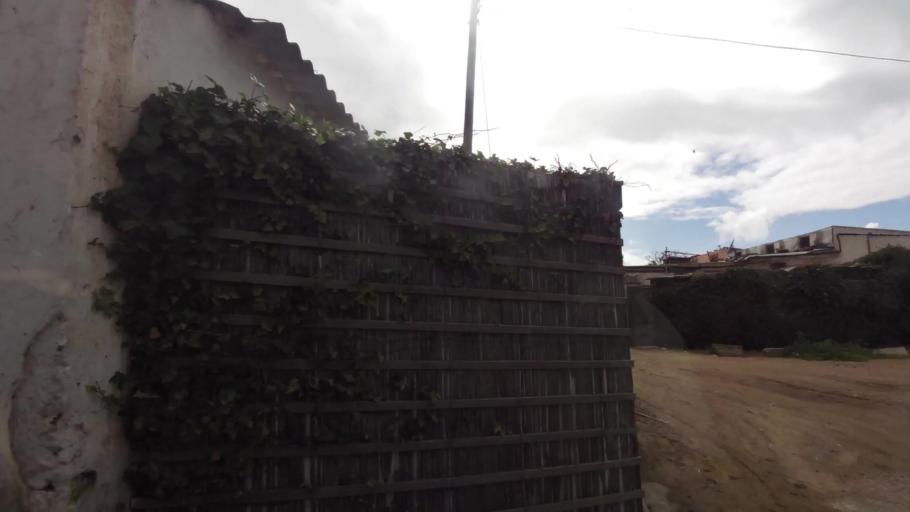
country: MA
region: Grand Casablanca
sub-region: Casablanca
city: Casablanca
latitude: 33.6075
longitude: -7.6524
